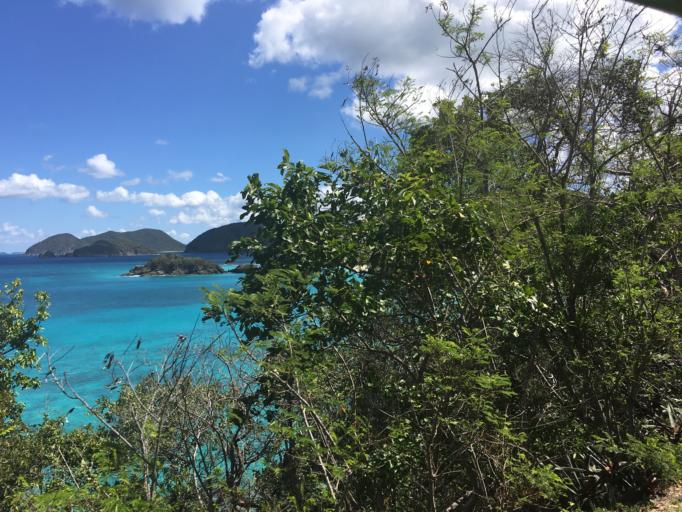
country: VI
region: Saint John Island
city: Cruz Bay
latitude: 18.3513
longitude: -64.7727
